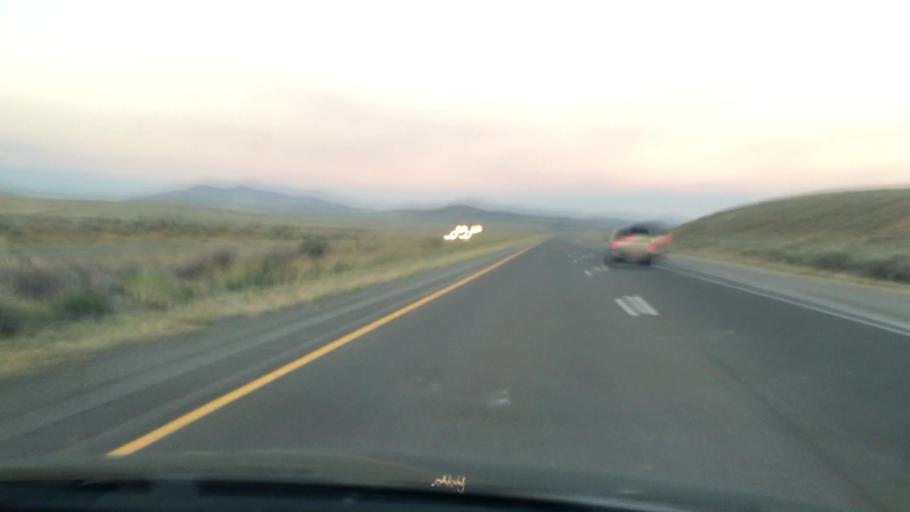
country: US
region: Idaho
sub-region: Power County
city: American Falls
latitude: 42.2613
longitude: -113.1297
